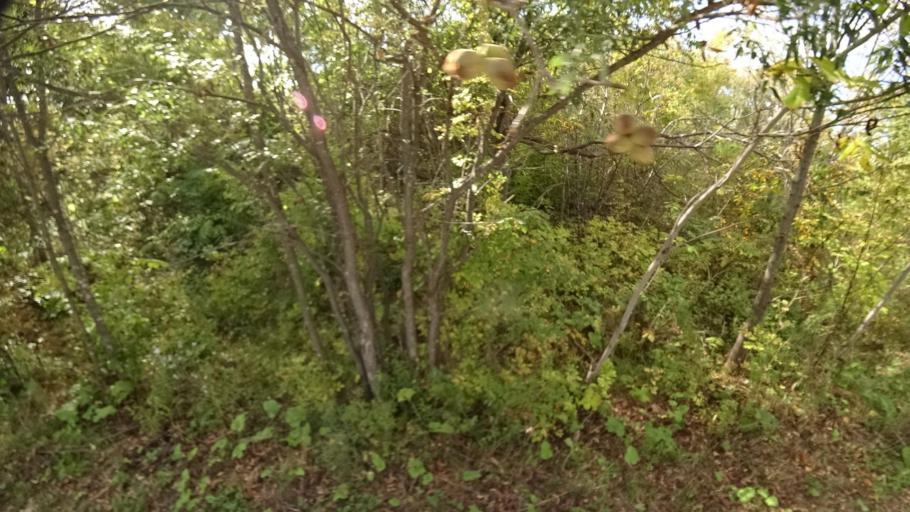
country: RU
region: Primorskiy
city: Dostoyevka
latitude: 44.2935
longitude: 133.4586
